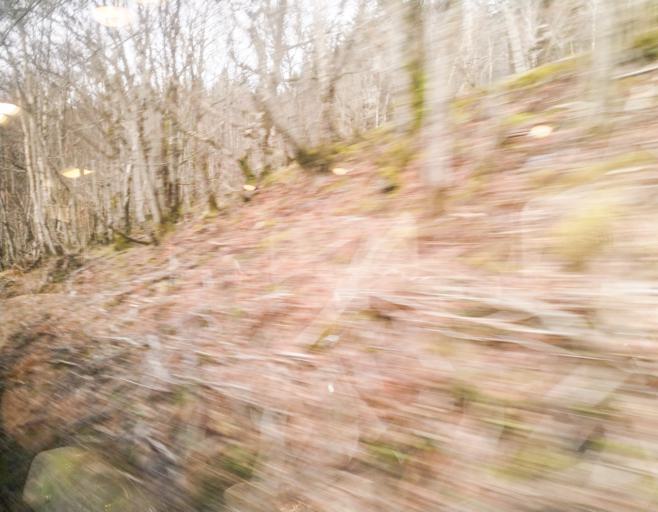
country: GB
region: Scotland
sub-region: Highland
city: Spean Bridge
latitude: 56.8852
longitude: -4.8072
